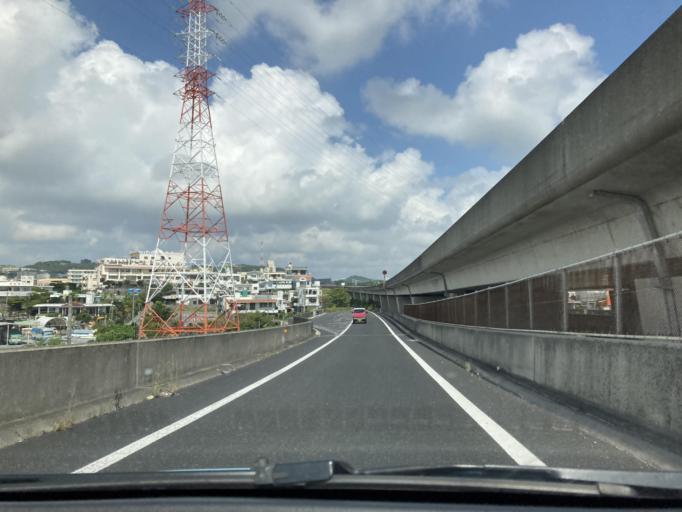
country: JP
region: Okinawa
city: Tomigusuku
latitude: 26.1959
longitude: 127.7396
